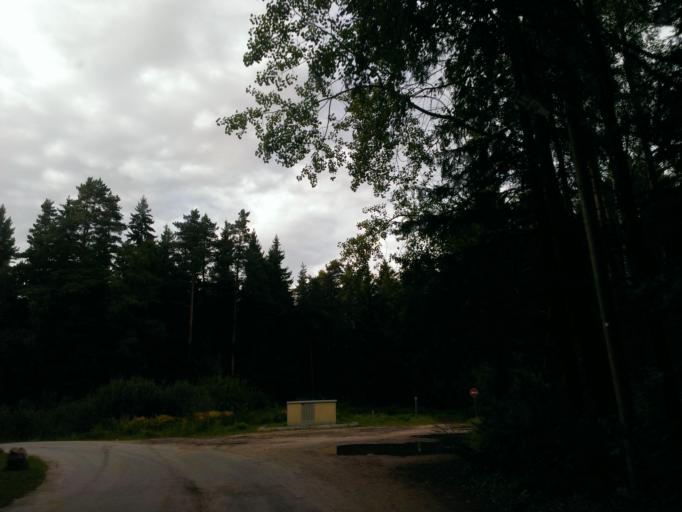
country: LV
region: Ogre
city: Ogre
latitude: 56.8276
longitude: 24.5829
